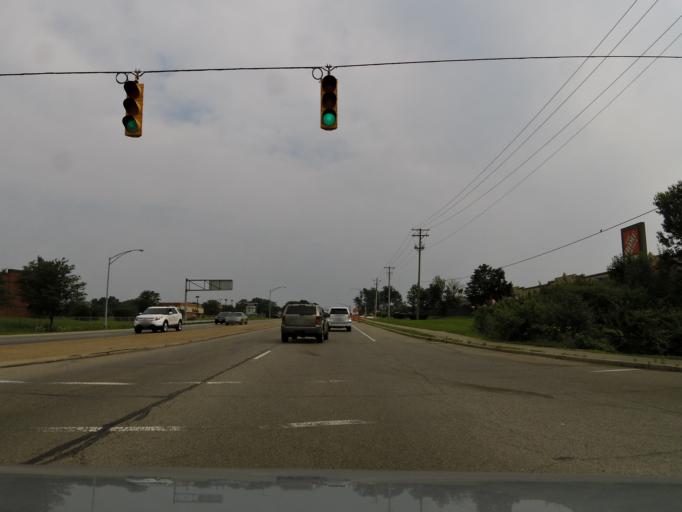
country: US
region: Ohio
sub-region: Greene County
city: Bellbrook
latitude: 39.6572
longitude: -84.1095
